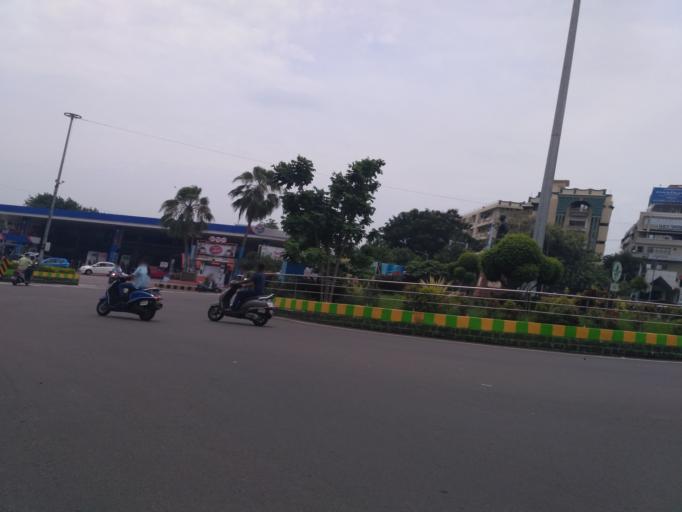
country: IN
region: Andhra Pradesh
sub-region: Vishakhapatnam
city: Yarada
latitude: 17.7212
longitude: 83.3201
